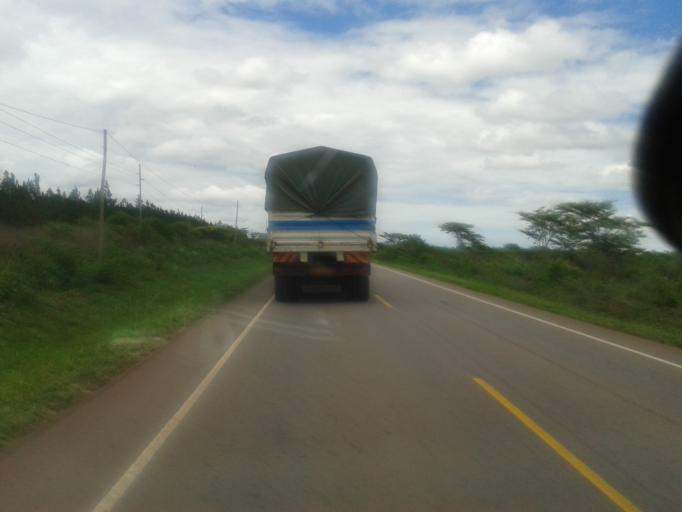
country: UG
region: Western Region
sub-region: Kiryandongo District
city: Masindi Port
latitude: 1.7492
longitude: 32.0224
